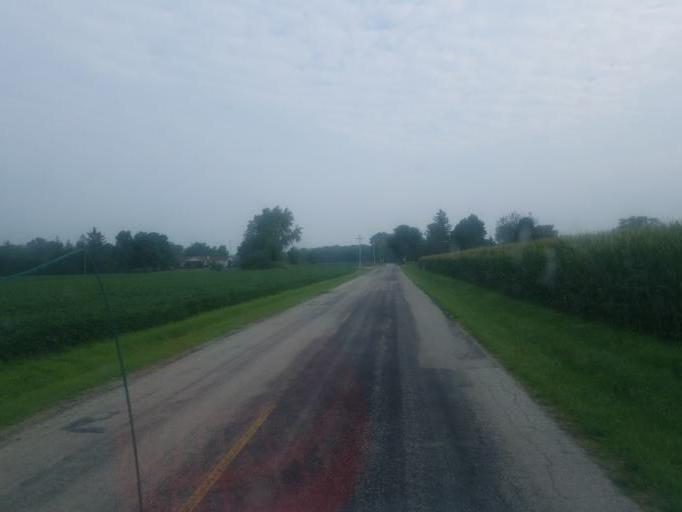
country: US
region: Ohio
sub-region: Morrow County
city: Cardington
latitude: 40.5842
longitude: -82.9765
